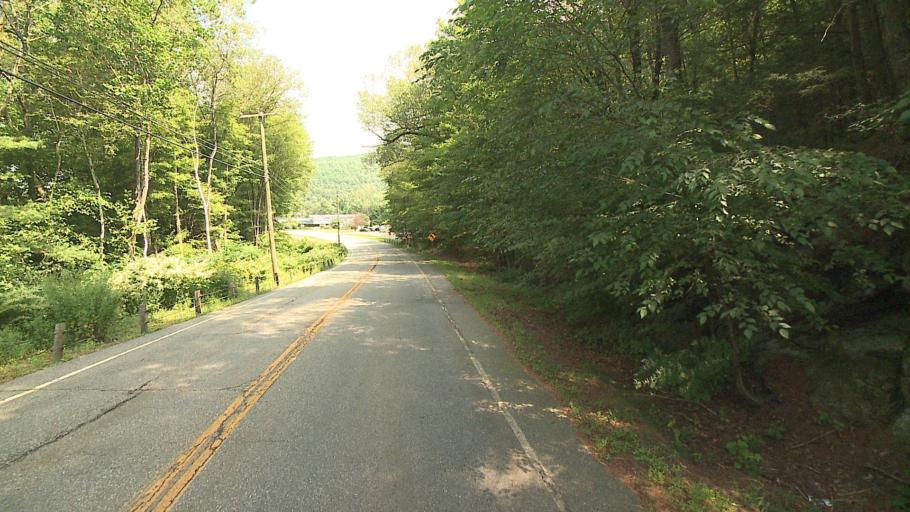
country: US
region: Connecticut
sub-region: Litchfield County
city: Oakville
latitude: 41.6327
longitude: -73.0771
